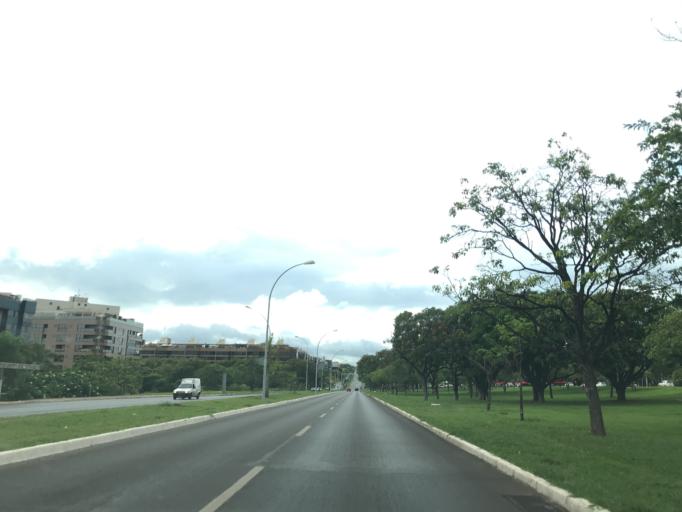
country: BR
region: Federal District
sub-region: Brasilia
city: Brasilia
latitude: -15.7462
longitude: -47.8886
